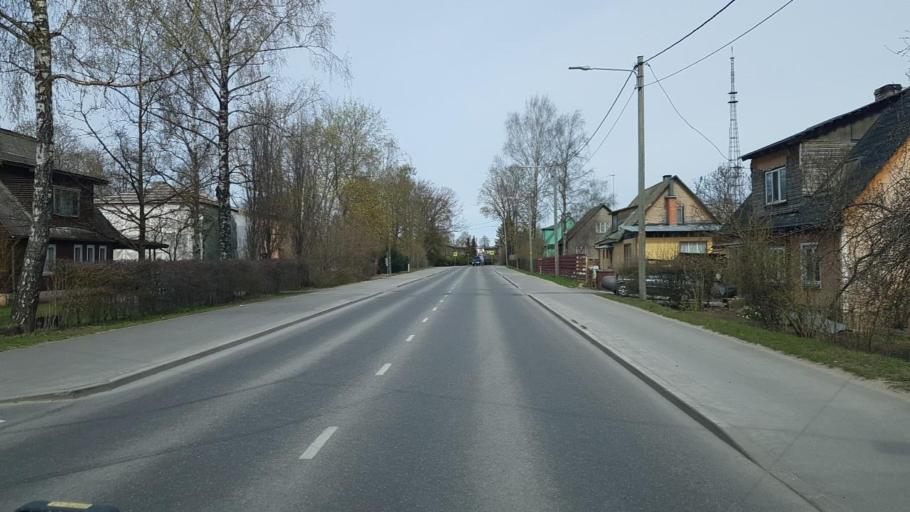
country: EE
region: Tartu
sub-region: Tartu linn
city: Tartu
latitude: 58.3560
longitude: 26.7063
